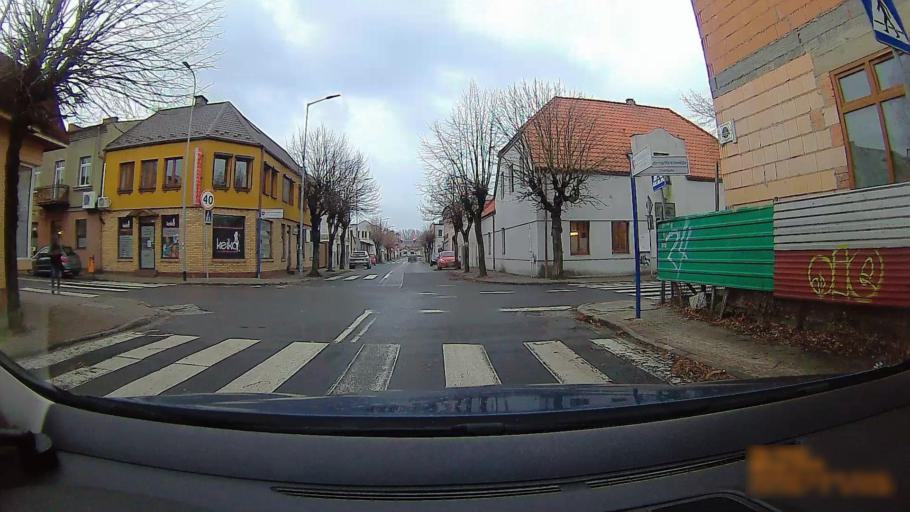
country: PL
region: Greater Poland Voivodeship
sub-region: Konin
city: Konin
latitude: 52.2111
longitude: 18.2510
